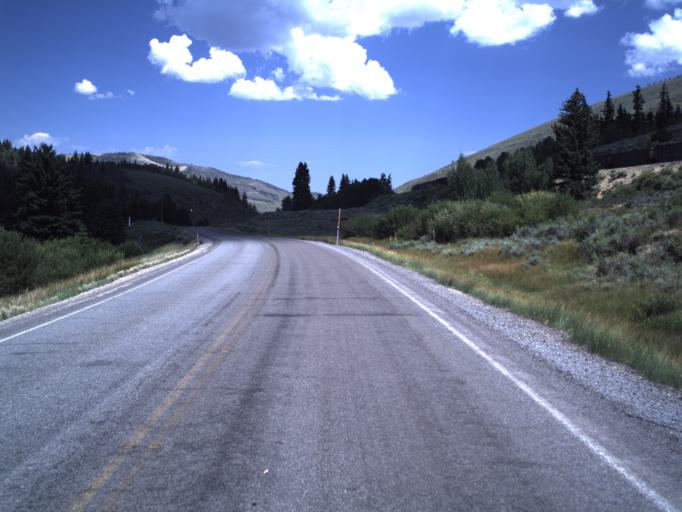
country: US
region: Utah
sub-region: Sanpete County
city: Fairview
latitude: 39.6919
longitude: -111.1552
